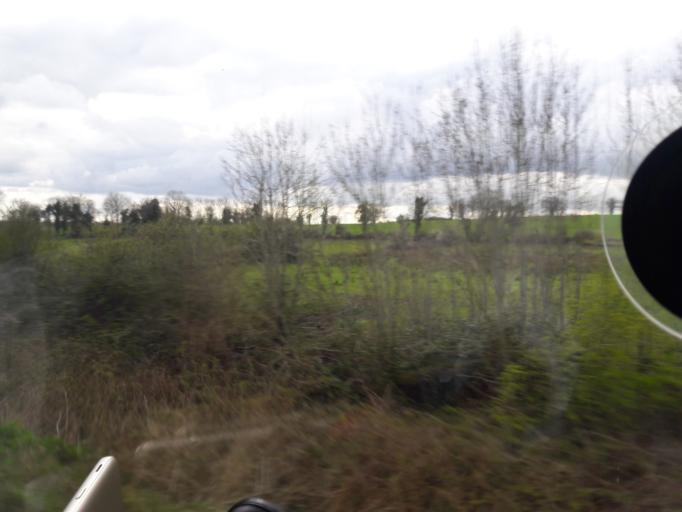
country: IE
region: Leinster
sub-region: An Longfort
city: Longford
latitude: 53.7295
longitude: -7.8185
